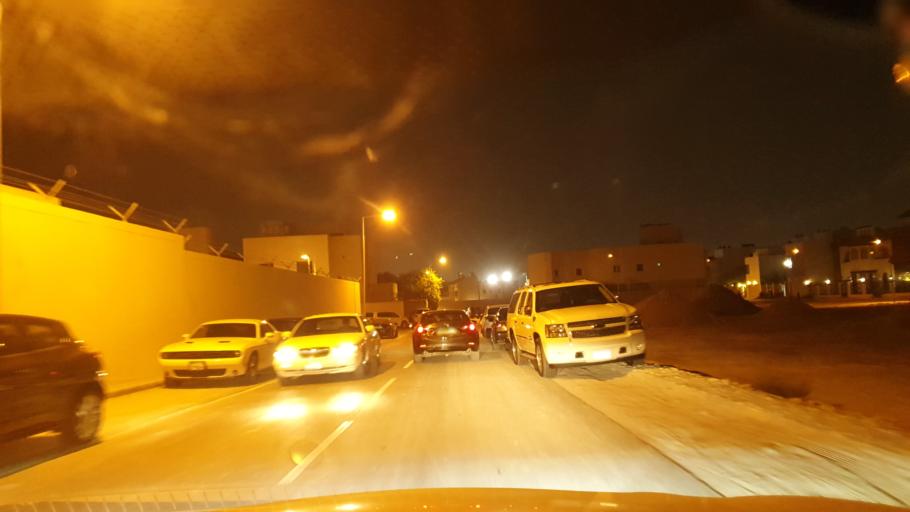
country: BH
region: Northern
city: Madinat `Isa
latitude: 26.1954
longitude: 50.4889
